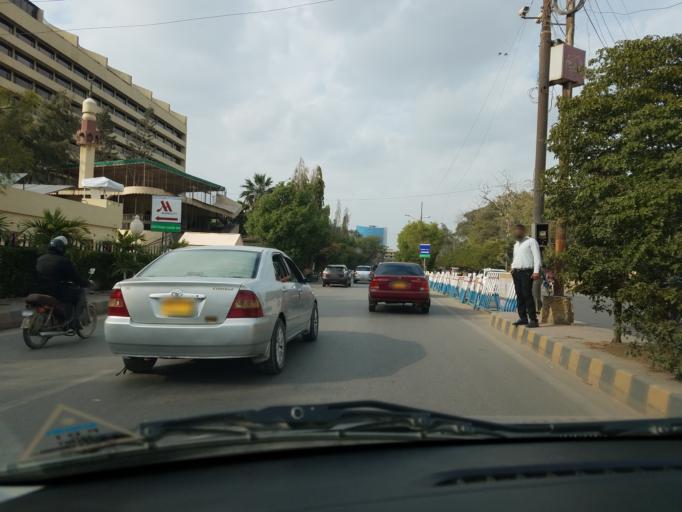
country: PK
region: Sindh
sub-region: Karachi District
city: Karachi
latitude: 24.8456
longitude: 67.0318
